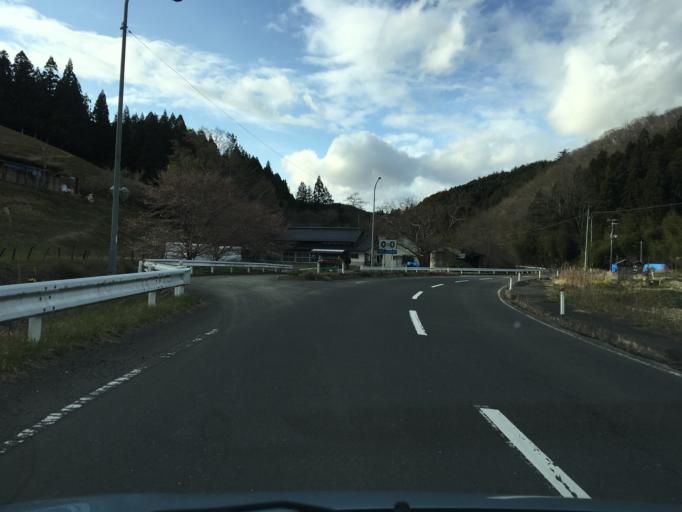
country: JP
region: Iwate
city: Ichinoseki
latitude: 38.8002
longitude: 141.3177
